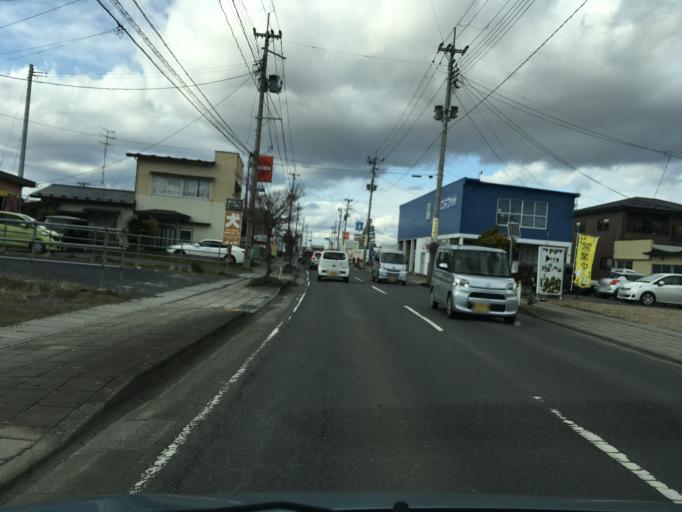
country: JP
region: Miyagi
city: Wakuya
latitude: 38.6785
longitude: 141.1946
